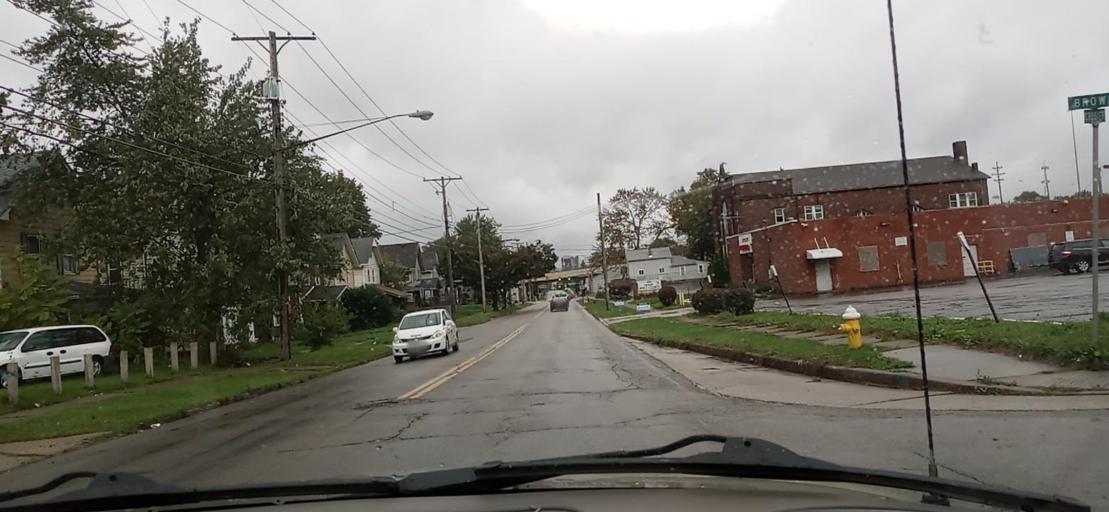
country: US
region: Ohio
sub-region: Summit County
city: Akron
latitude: 41.0598
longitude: -81.5098
